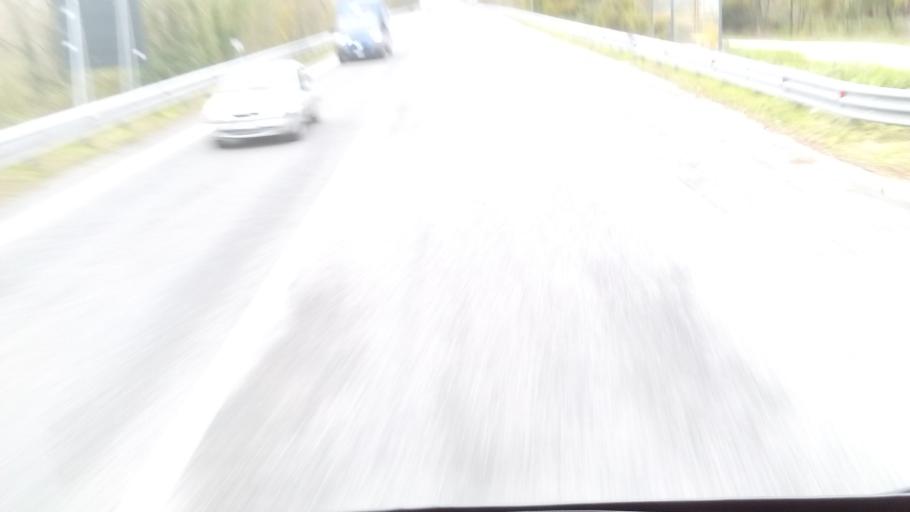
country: IT
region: Molise
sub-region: Provincia di Isernia
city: Sessano del Molise
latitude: 41.6379
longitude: 14.3212
